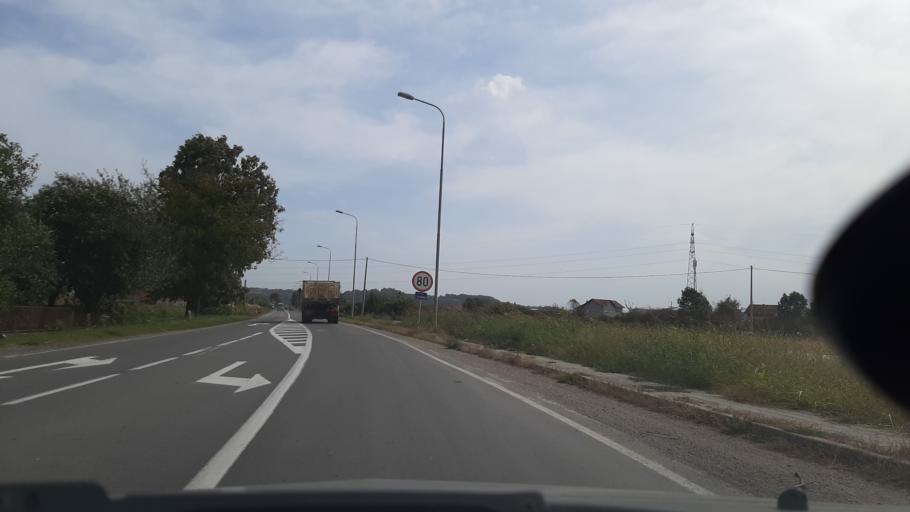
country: BA
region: Republika Srpska
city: Laktasi
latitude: 44.8780
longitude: 17.2919
